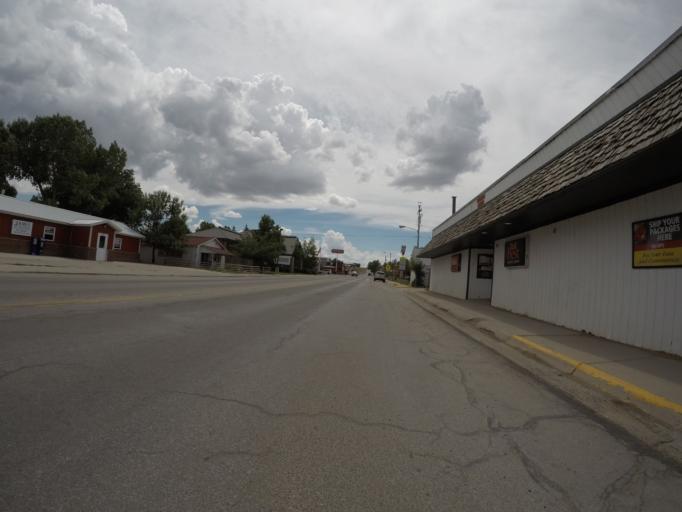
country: US
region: Wyoming
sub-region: Carbon County
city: Saratoga
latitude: 41.4539
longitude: -106.8077
